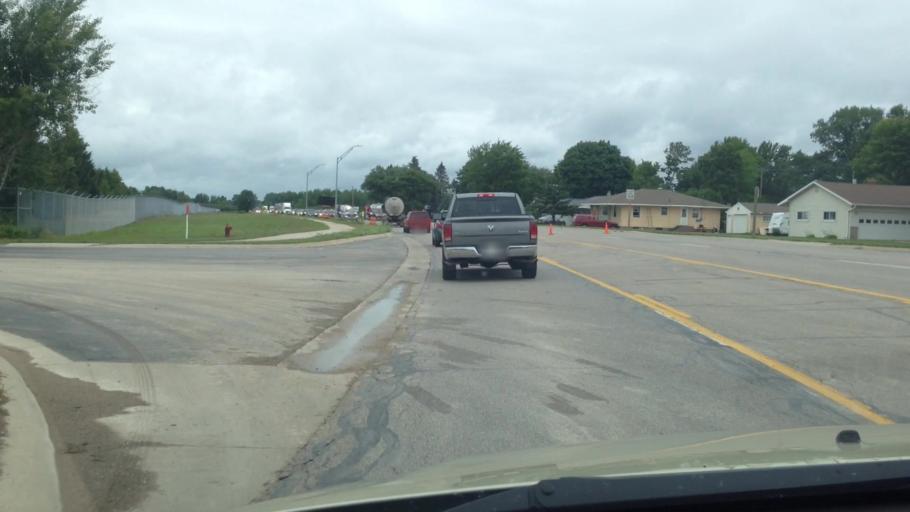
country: US
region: Michigan
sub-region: Delta County
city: Escanaba
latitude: 45.7171
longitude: -87.0805
